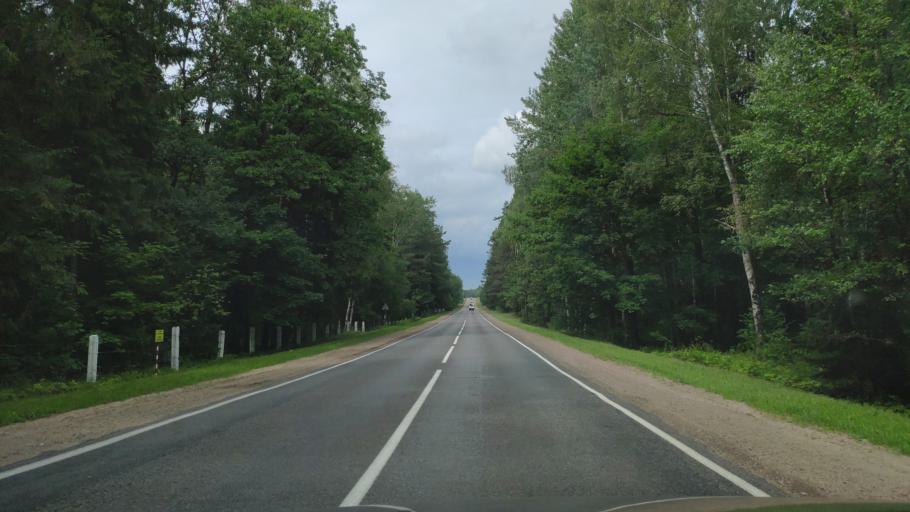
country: BY
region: Minsk
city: Novosel'ye
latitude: 53.9527
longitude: 27.2459
